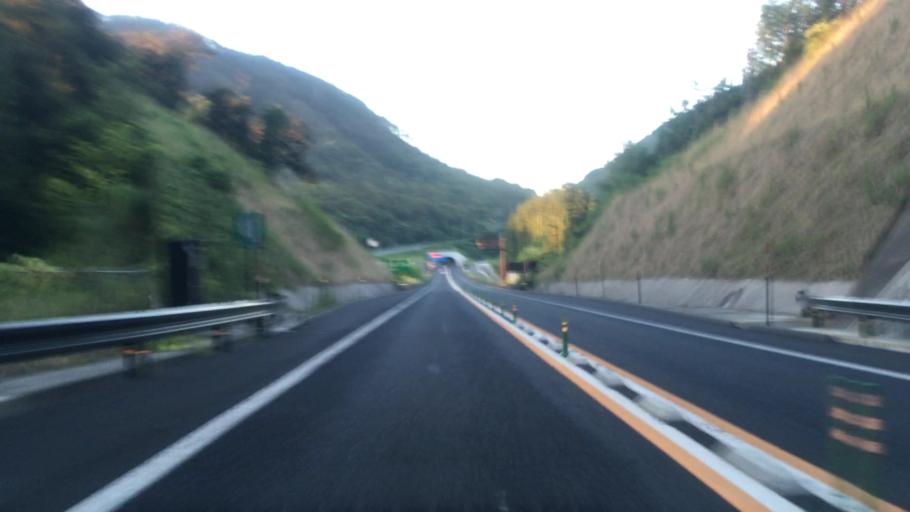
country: JP
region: Tottori
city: Tottori
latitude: 35.5569
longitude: 134.2823
